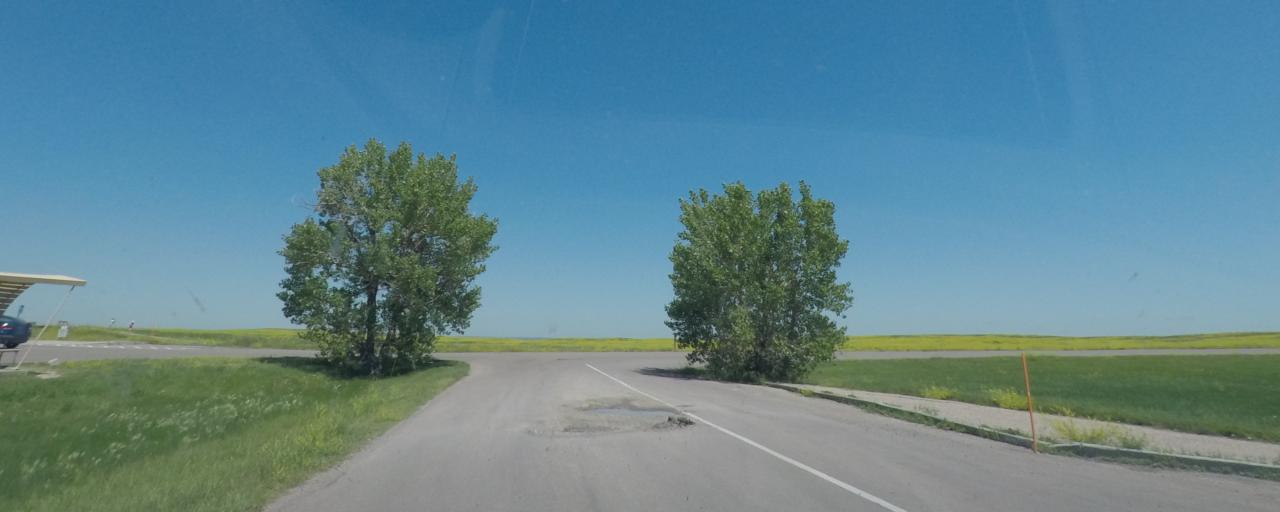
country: US
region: South Dakota
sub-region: Haakon County
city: Philip
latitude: 43.7951
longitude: -102.0448
